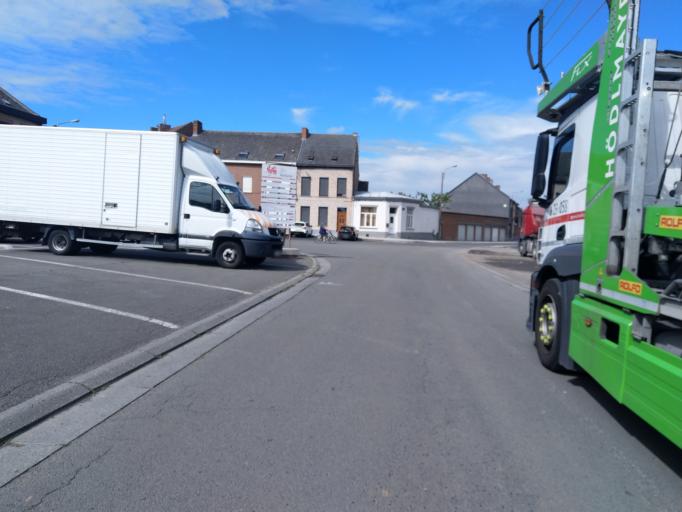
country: BE
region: Wallonia
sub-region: Province du Hainaut
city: Quievrain
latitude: 50.4098
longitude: 3.6863
